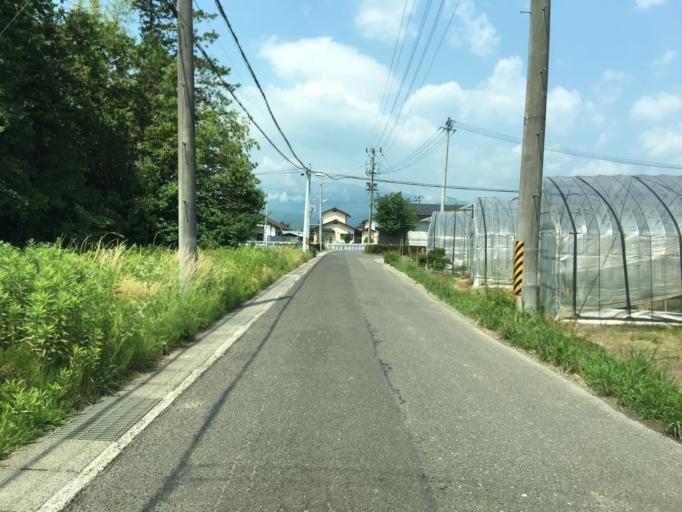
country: JP
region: Fukushima
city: Fukushima-shi
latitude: 37.7391
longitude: 140.4335
